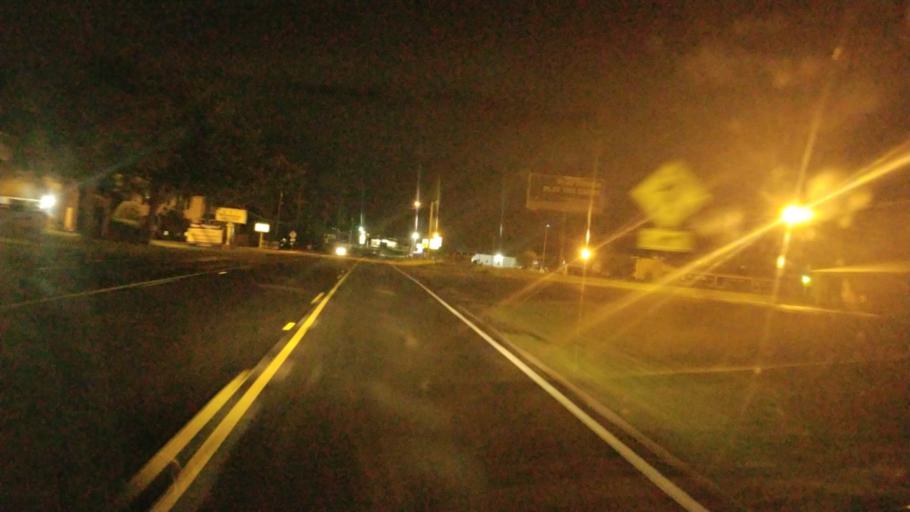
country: US
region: Ohio
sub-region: Trumbull County
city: McKinley Heights
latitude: 41.1867
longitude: -80.7226
